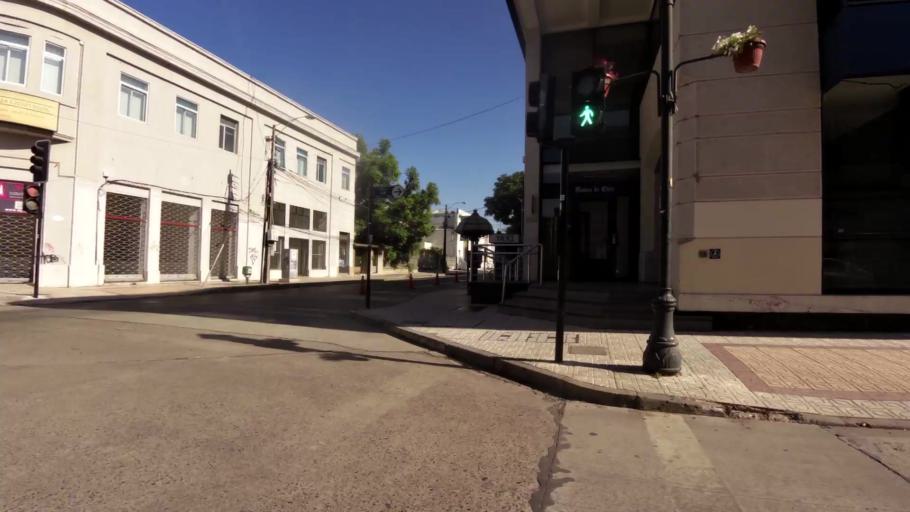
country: CL
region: Maule
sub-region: Provincia de Talca
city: Talca
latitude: -35.4274
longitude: -71.6627
